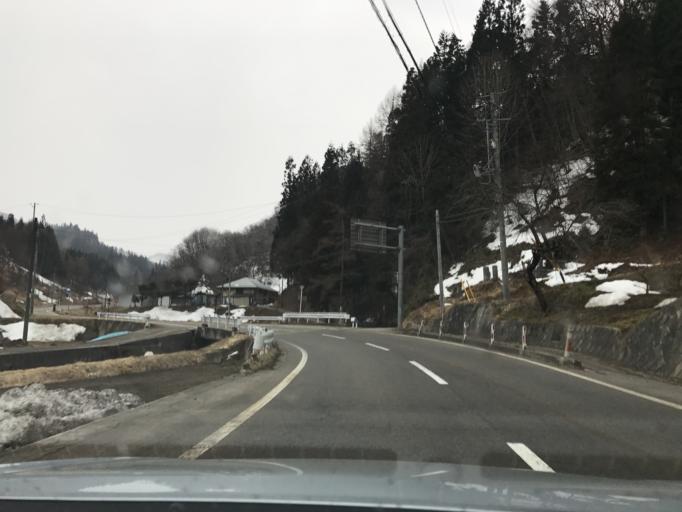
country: JP
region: Nagano
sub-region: Kitaazumi Gun
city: Hakuba
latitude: 36.6050
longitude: 137.8881
